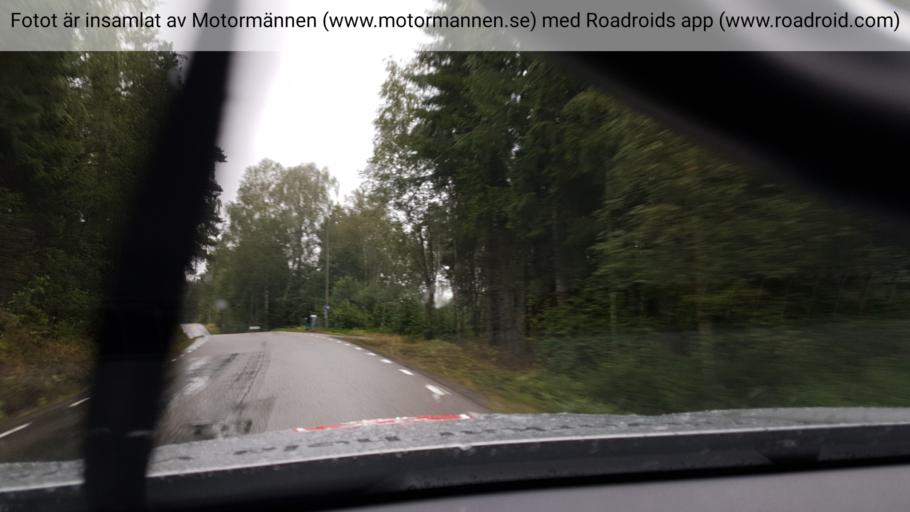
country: SE
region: Vaestra Goetaland
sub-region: Harryda Kommun
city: Hindas
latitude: 57.7343
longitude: 12.4927
